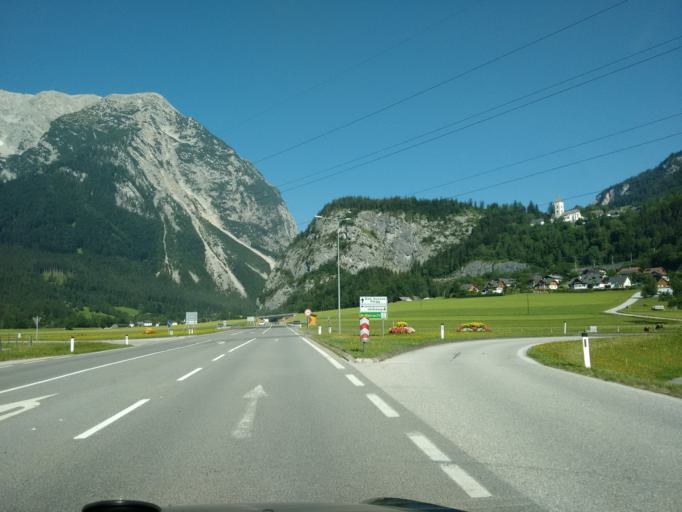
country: AT
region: Styria
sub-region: Politischer Bezirk Liezen
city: Irdning
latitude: 47.5245
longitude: 14.0738
